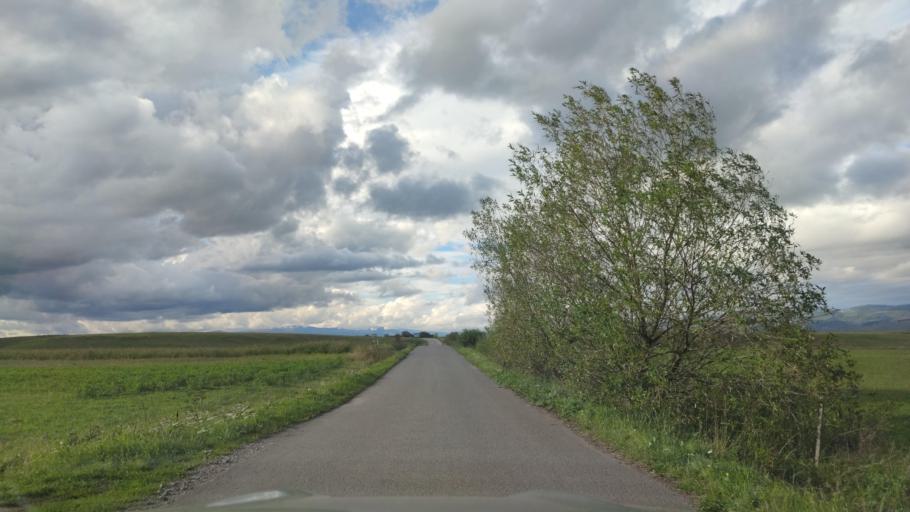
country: RO
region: Harghita
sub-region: Comuna Remetea
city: Remetea
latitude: 46.8123
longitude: 25.4357
